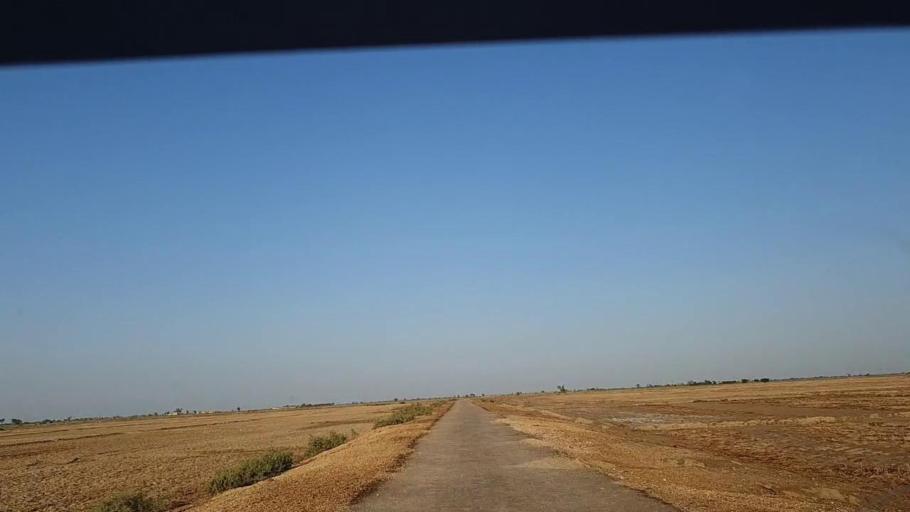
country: PK
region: Sindh
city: Johi
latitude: 26.7444
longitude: 67.6230
